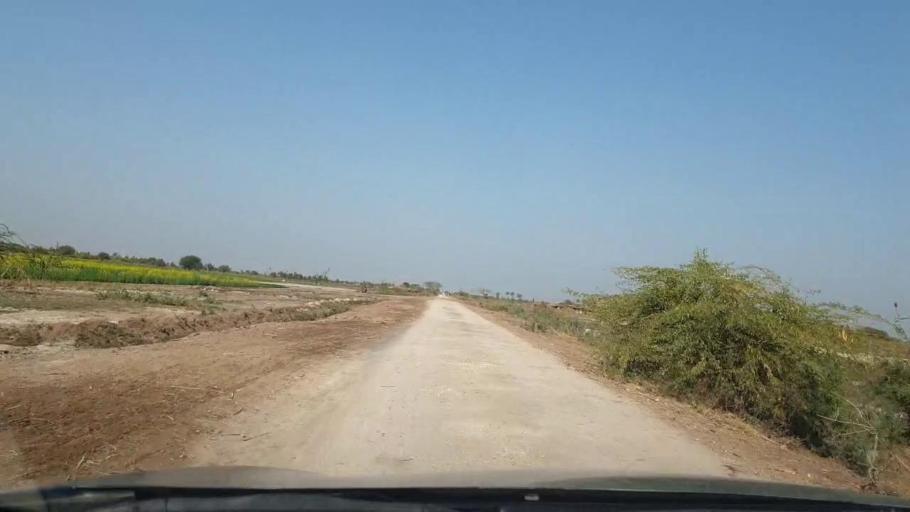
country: PK
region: Sindh
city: Mirpur Khas
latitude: 25.6045
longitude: 68.8901
